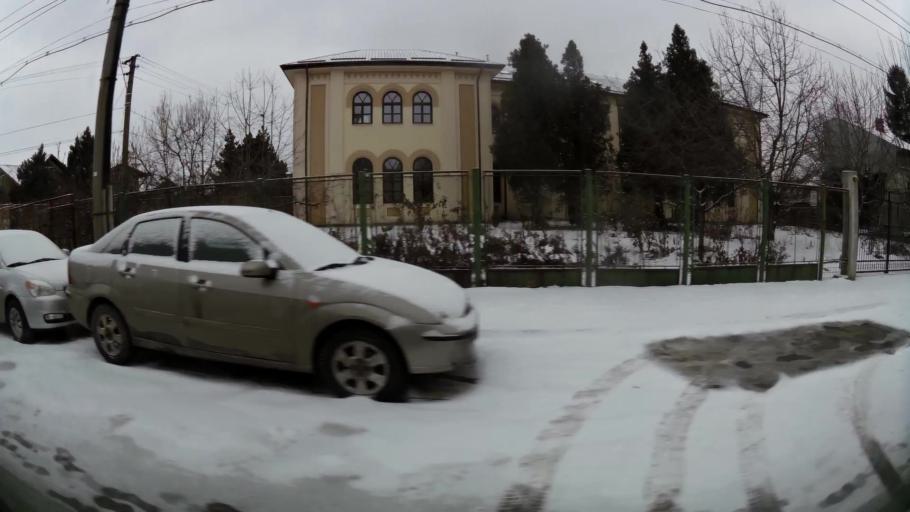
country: RO
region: Prahova
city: Ploiesti
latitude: 44.9381
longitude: 26.0392
